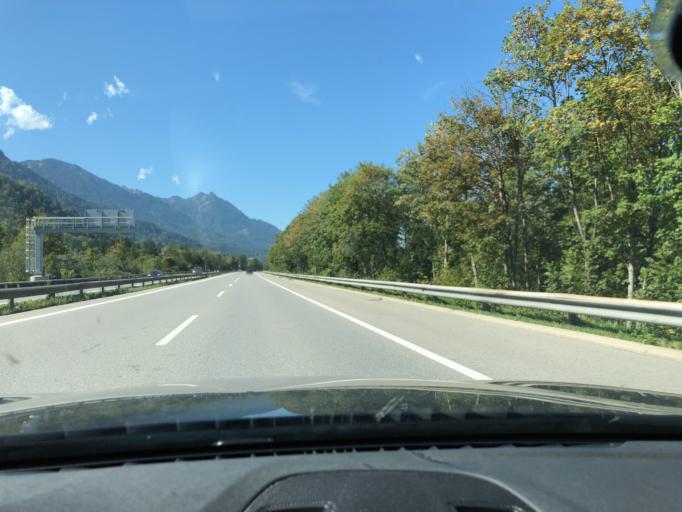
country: AT
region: Vorarlberg
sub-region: Politischer Bezirk Bludenz
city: Bludesch
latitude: 47.1761
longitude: 9.7455
